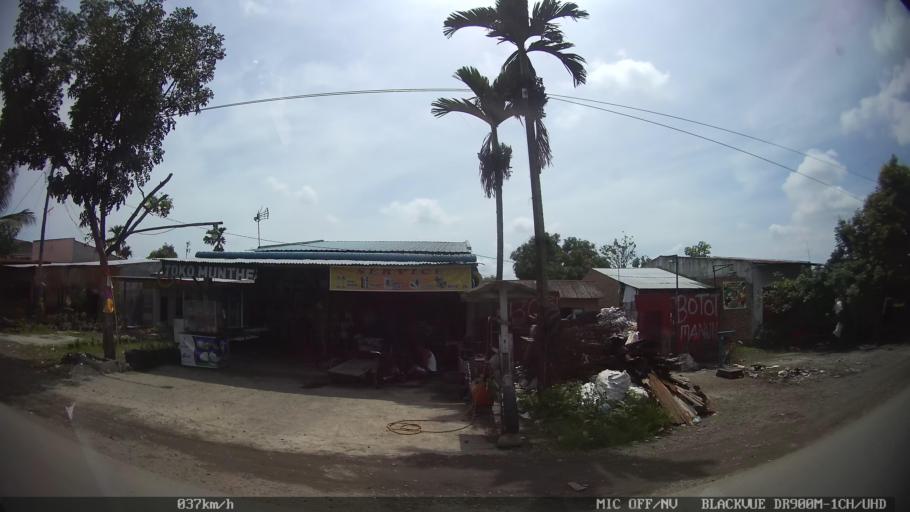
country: ID
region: North Sumatra
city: Medan
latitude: 3.6458
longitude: 98.7087
